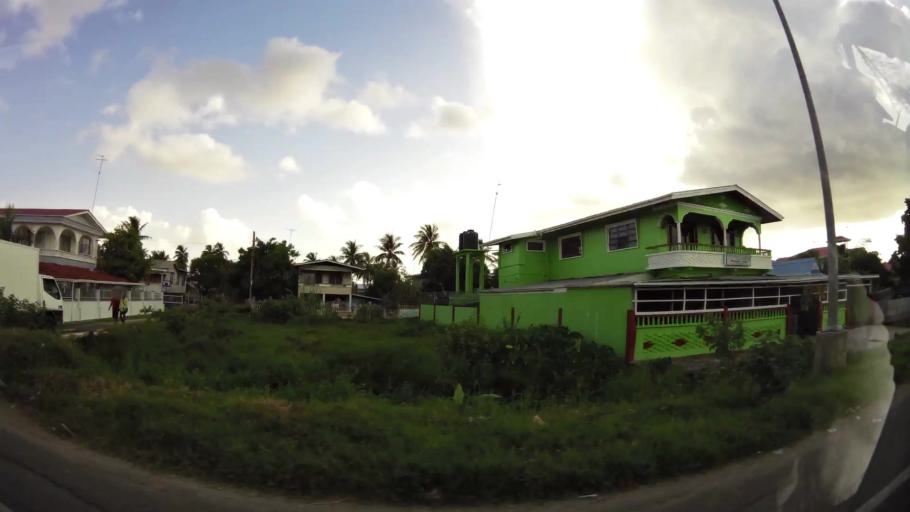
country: GY
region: Demerara-Mahaica
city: Georgetown
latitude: 6.7936
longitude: -58.0307
